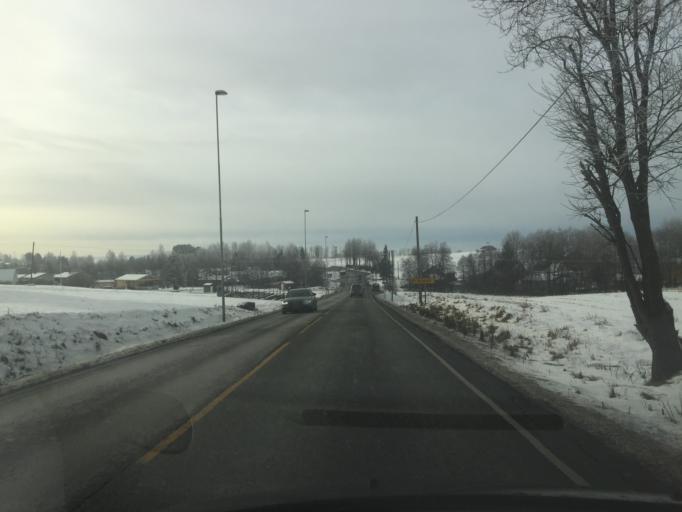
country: NO
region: Hedmark
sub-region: Loten
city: Loten
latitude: 60.8357
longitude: 11.3571
